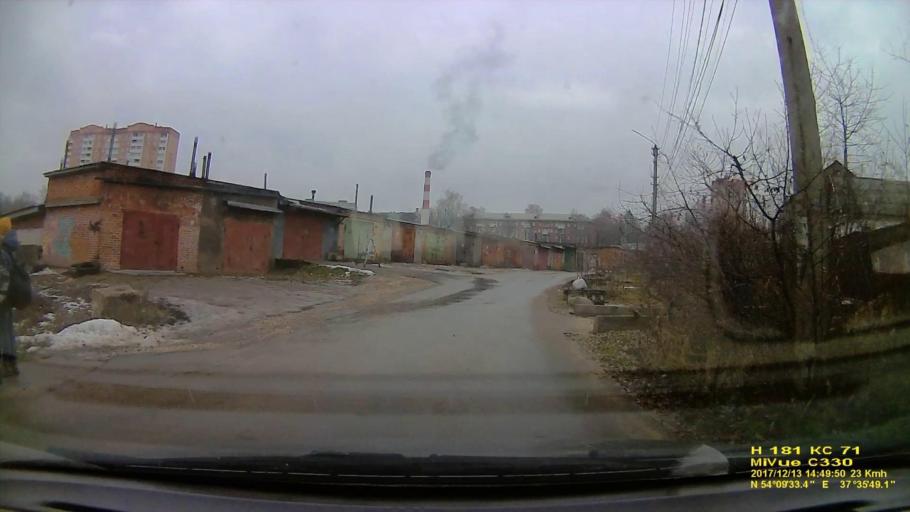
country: RU
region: Tula
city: Mendeleyevskiy
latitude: 54.1593
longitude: 37.5968
